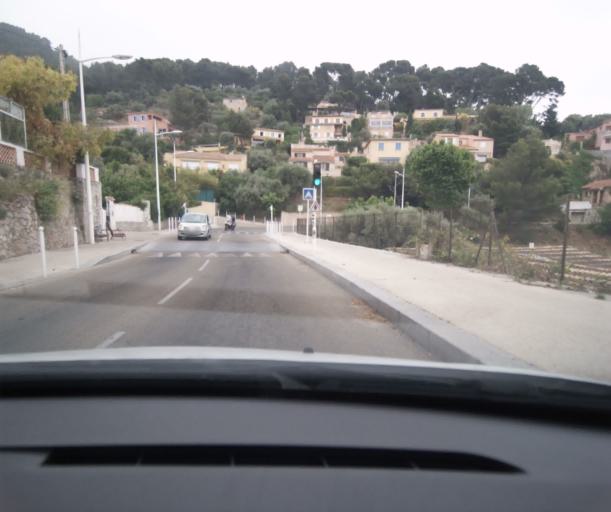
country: FR
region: Provence-Alpes-Cote d'Azur
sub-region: Departement du Var
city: Toulon
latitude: 43.1332
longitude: 5.9534
